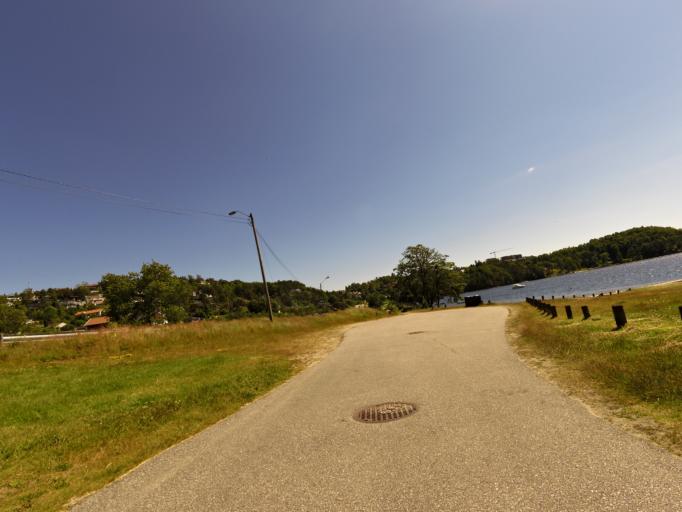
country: NO
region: Vest-Agder
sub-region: Kristiansand
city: Justvik
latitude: 58.1902
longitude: 8.0840
